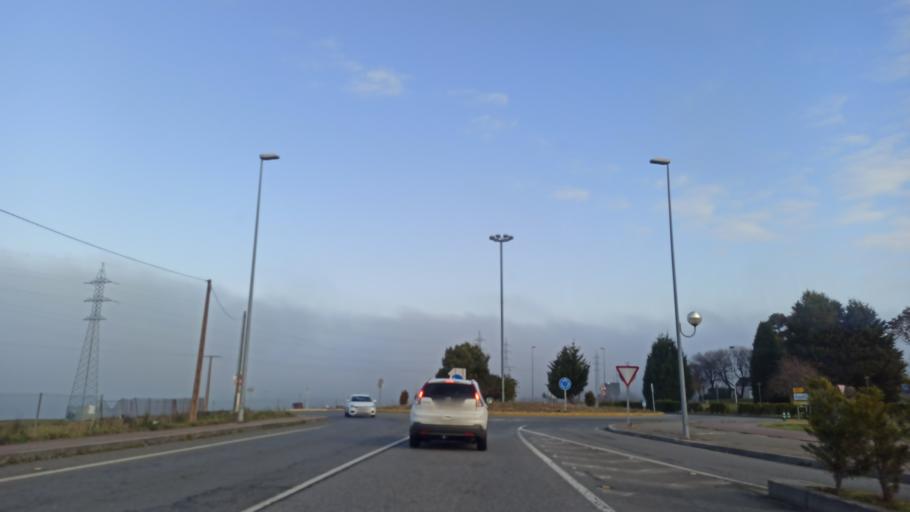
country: ES
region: Galicia
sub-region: Provincia da Coruna
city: As Pontes de Garcia Rodriguez
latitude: 43.4524
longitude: -7.8680
